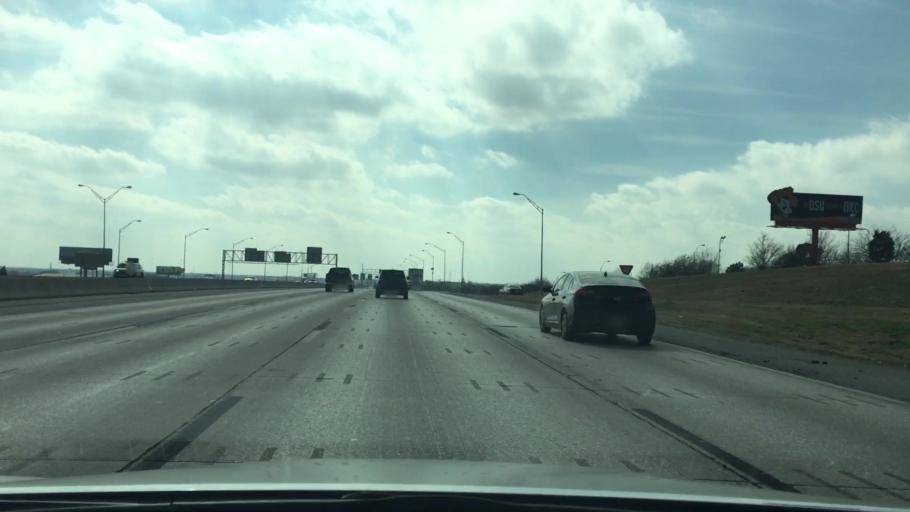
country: US
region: Oklahoma
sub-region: Oklahoma County
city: Warr Acres
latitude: 35.4761
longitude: -97.5791
